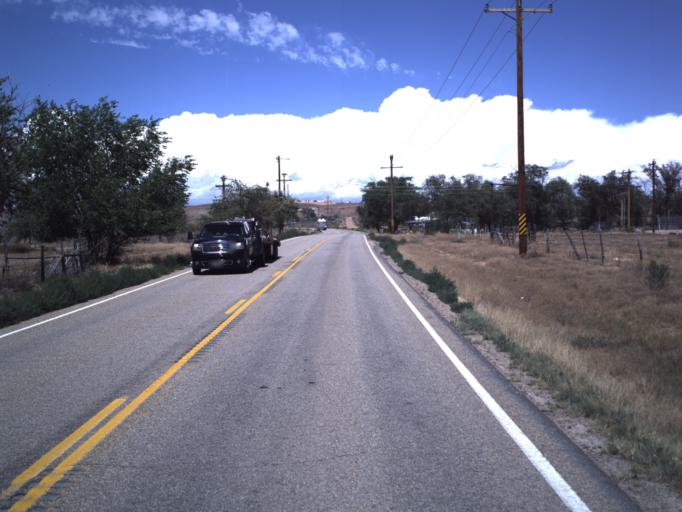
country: US
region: Utah
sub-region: Uintah County
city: Naples
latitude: 40.2022
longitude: -109.6649
